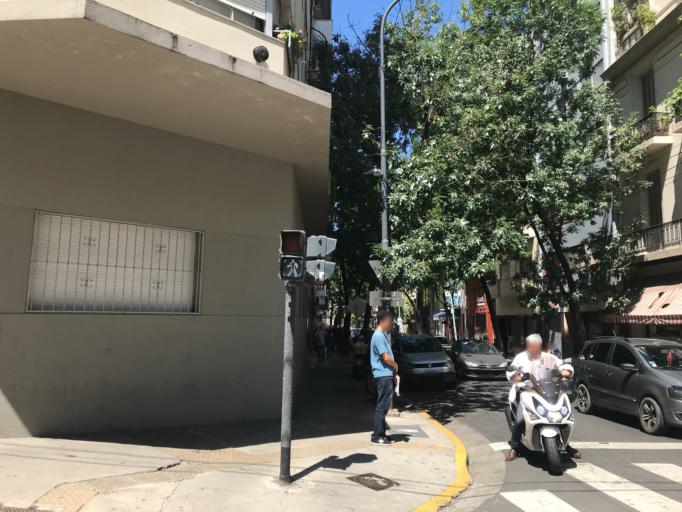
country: AR
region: Buenos Aires F.D.
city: Buenos Aires
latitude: -34.6021
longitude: -58.3985
